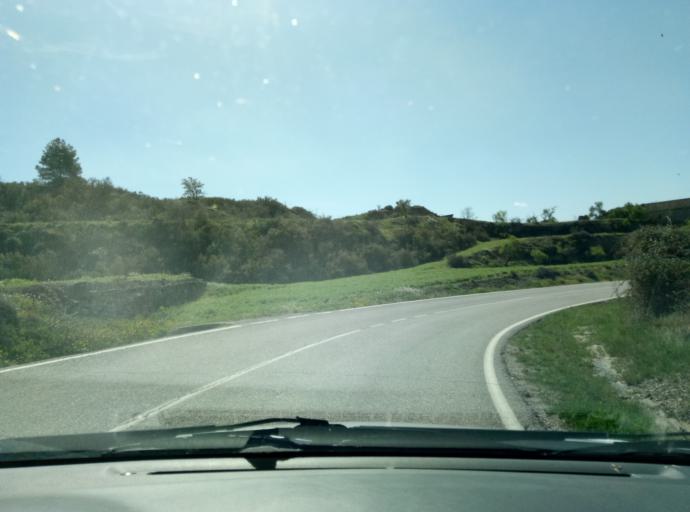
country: ES
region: Catalonia
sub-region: Provincia de Lleida
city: Fulleda
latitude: 41.4985
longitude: 1.0053
